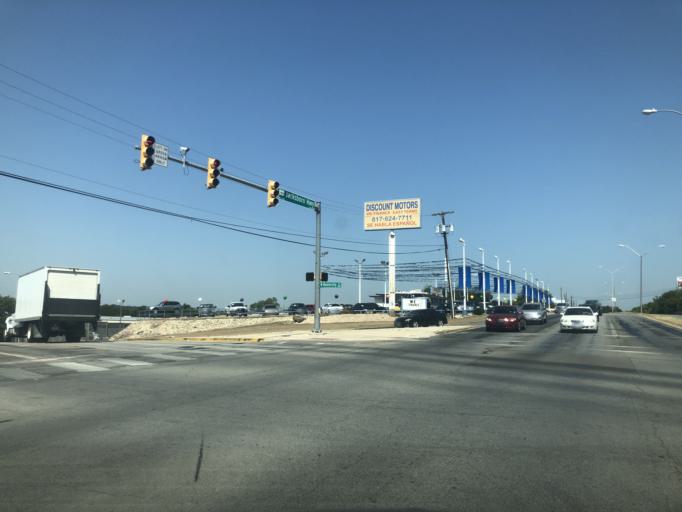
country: US
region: Texas
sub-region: Tarrant County
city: River Oaks
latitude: 32.7687
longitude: -97.3566
